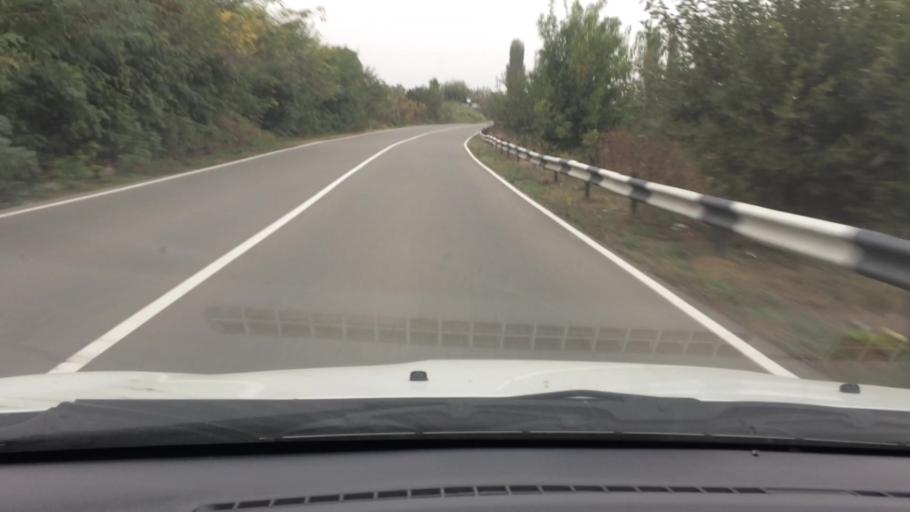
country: AM
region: Tavush
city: Bagratashen
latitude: 41.2745
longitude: 44.7905
